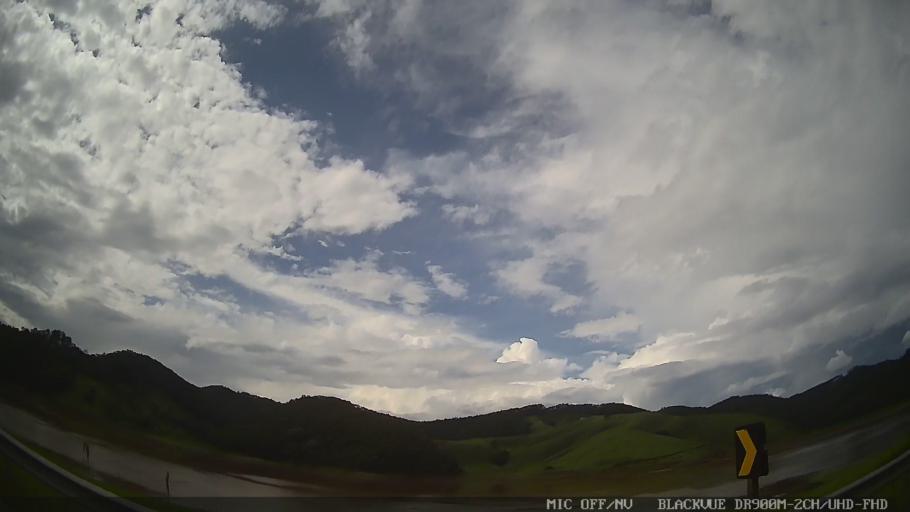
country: BR
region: Sao Paulo
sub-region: Santa Branca
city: Santa Branca
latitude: -23.5193
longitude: -45.8919
